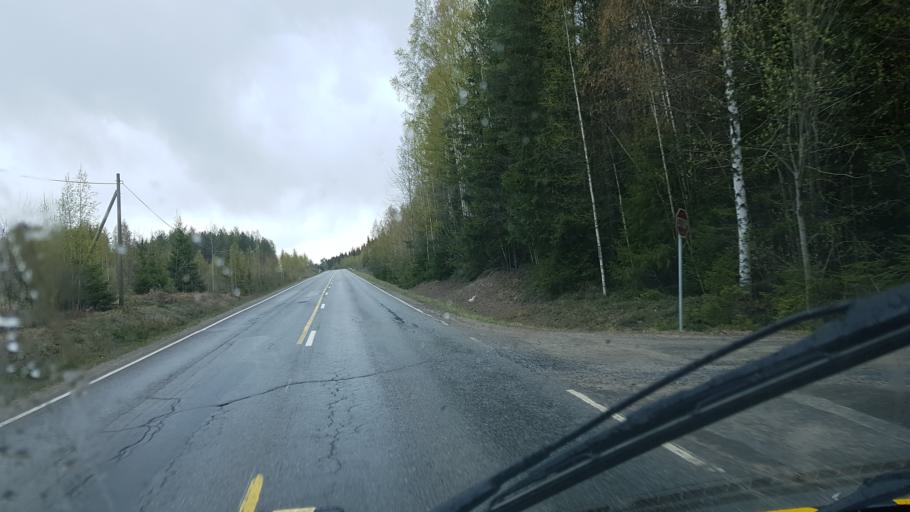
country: FI
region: Pirkanmaa
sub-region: Tampere
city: Pirkkala
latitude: 61.4019
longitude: 23.6306
